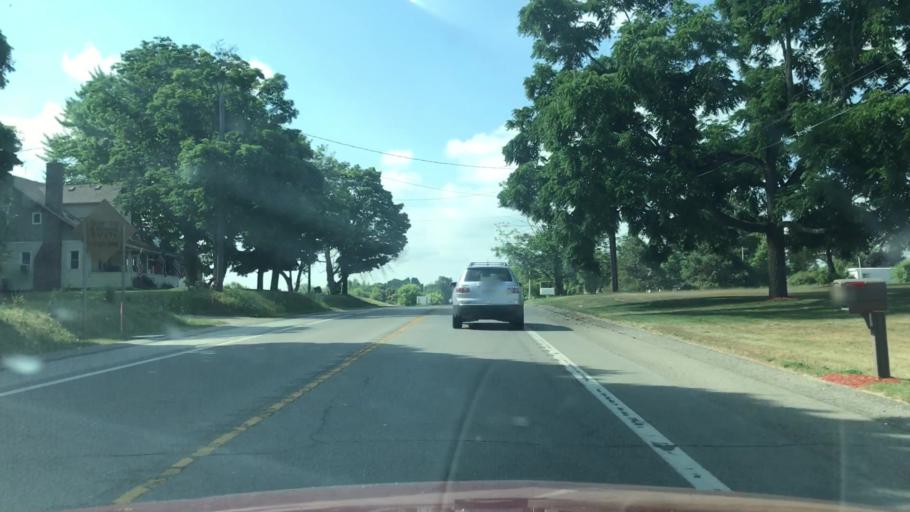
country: US
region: Michigan
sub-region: Newaygo County
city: Newaygo
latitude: 43.3167
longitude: -85.8106
